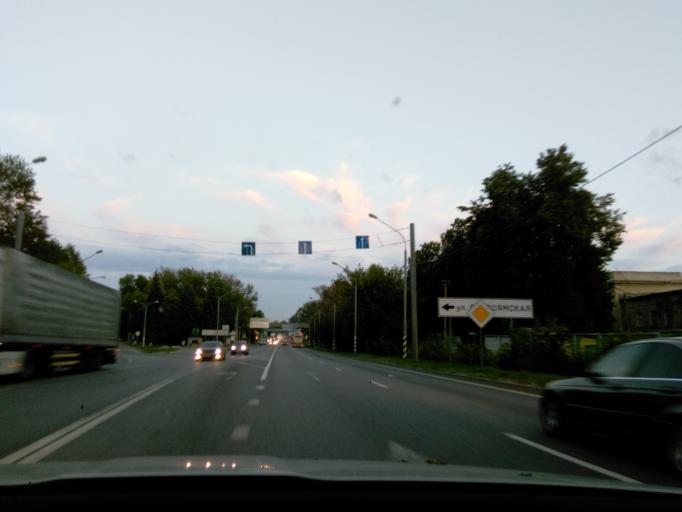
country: RU
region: Moskovskaya
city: Klin
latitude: 56.3409
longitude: 36.7137
